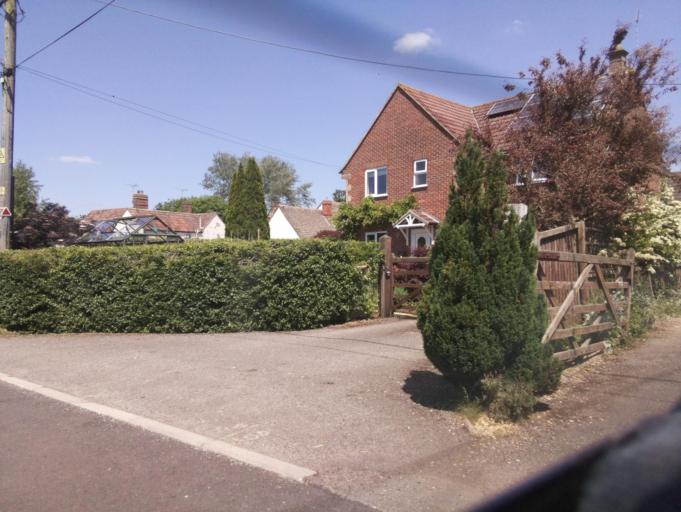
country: GB
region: England
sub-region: Wiltshire
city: Bremhill
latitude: 51.5078
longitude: -2.0521
